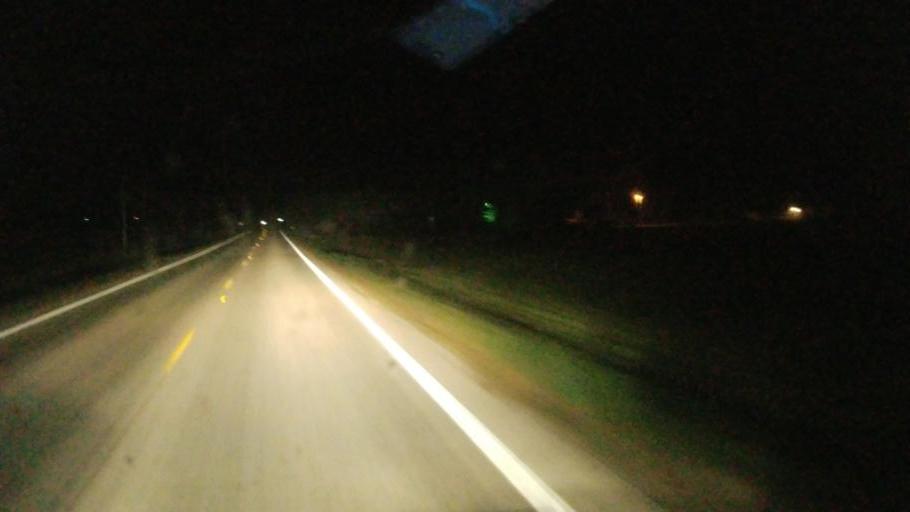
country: US
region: Ohio
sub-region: Union County
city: Richwood
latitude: 40.5765
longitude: -83.3401
